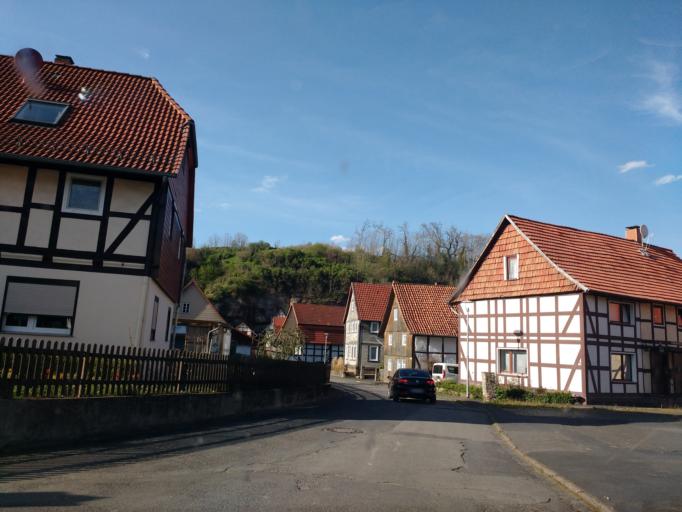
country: DE
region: Thuringia
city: Rohrberg
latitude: 51.4664
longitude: 9.9900
